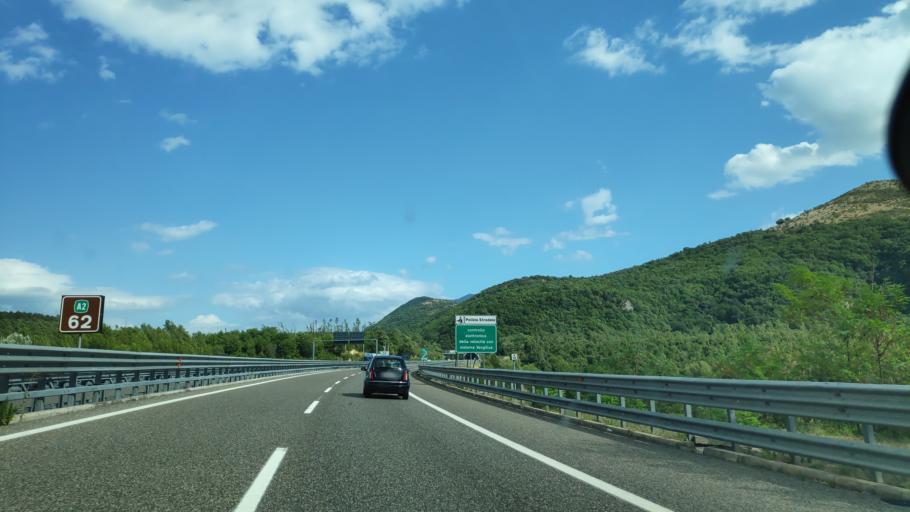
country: IT
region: Campania
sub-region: Provincia di Salerno
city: Sicignano degli Alburni
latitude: 40.6090
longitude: 15.2959
